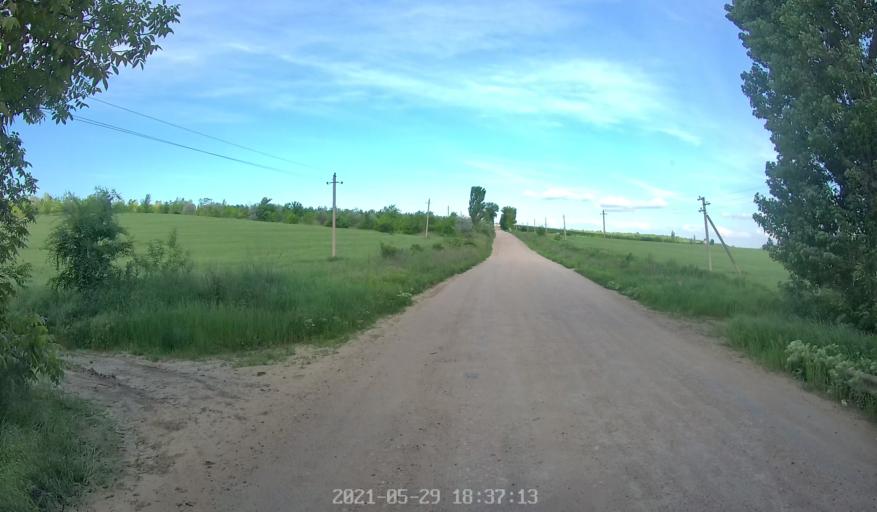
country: MD
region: Chisinau
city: Singera
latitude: 46.8047
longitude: 28.9294
